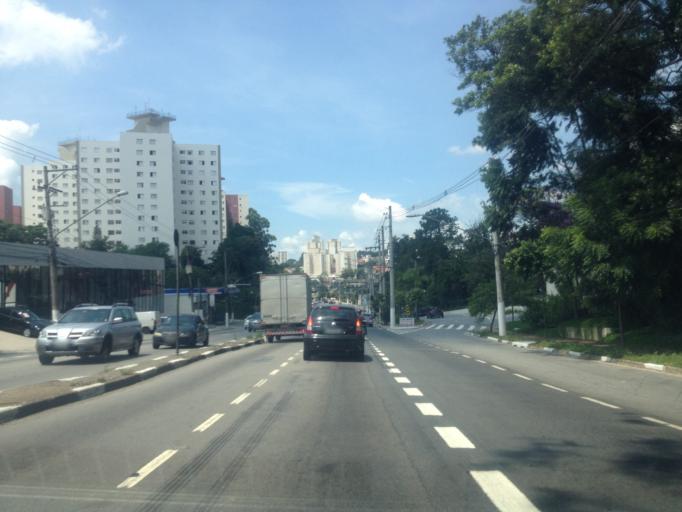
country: BR
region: Sao Paulo
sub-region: Diadema
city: Diadema
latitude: -23.6589
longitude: -46.6796
